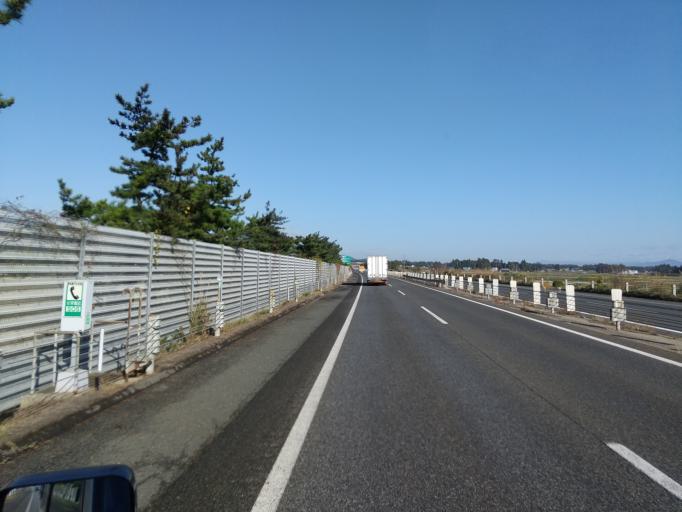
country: JP
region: Iwate
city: Hanamaki
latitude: 39.4524
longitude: 141.1099
